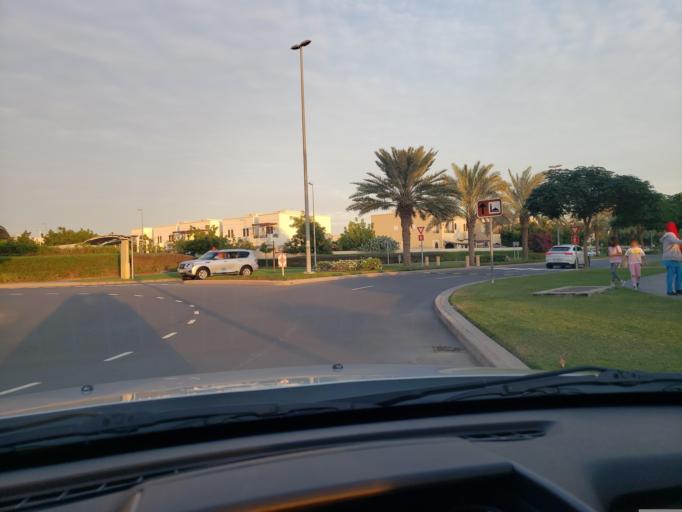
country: AE
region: Dubai
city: Dubai
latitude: 25.0265
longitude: 55.2671
